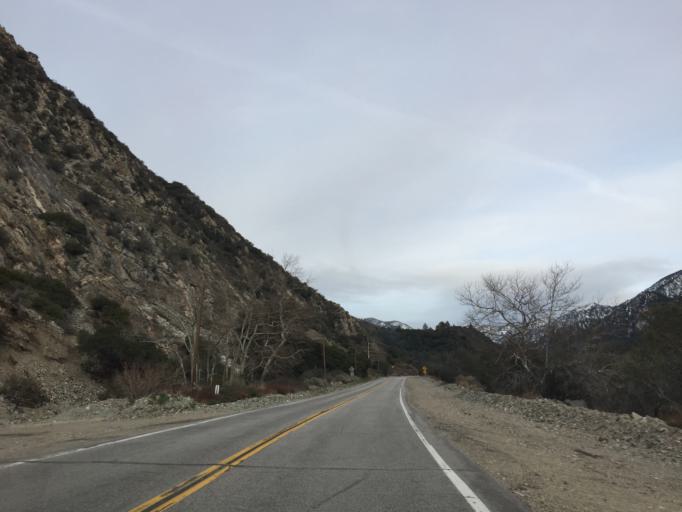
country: US
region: California
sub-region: San Bernardino County
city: Yucaipa
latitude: 34.0962
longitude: -116.9536
